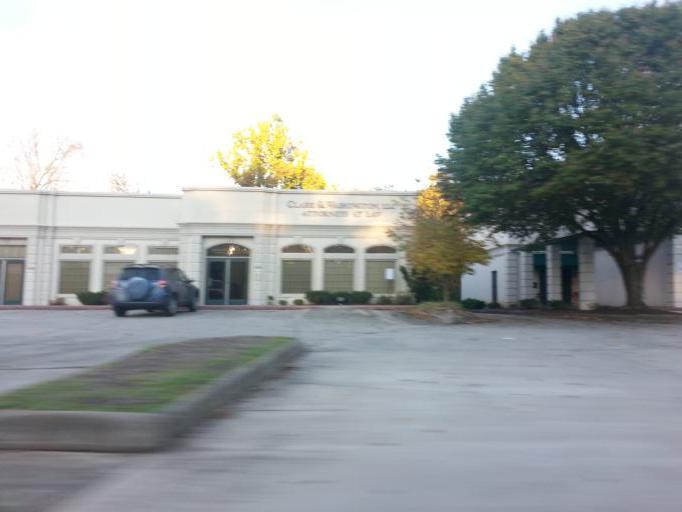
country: US
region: Tennessee
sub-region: Knox County
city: Knoxville
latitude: 35.9289
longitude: -84.0007
